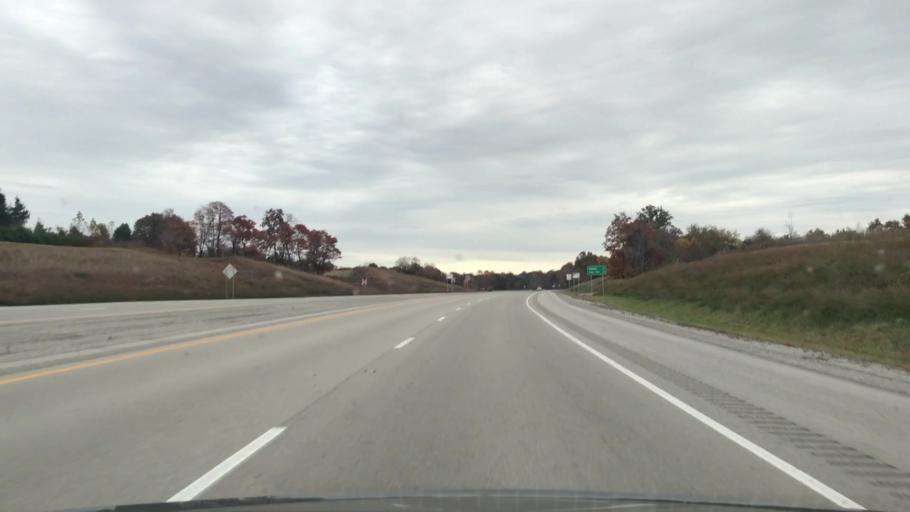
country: US
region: Kentucky
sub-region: Barren County
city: Glasgow
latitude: 36.9979
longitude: -85.9730
